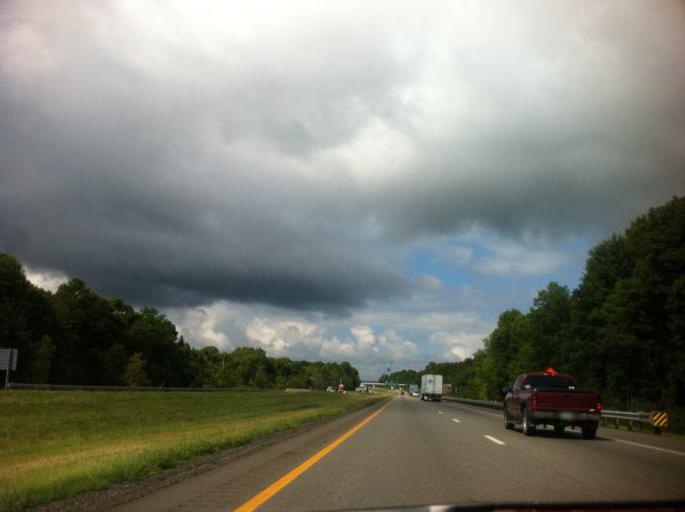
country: US
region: Ohio
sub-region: Trumbull County
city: Churchill
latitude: 41.1598
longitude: -80.6485
